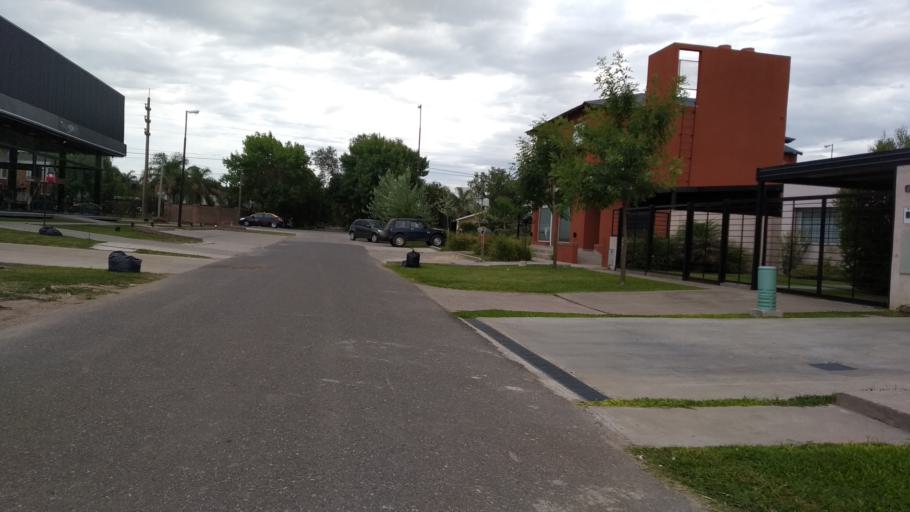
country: AR
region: Santa Fe
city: Funes
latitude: -32.9295
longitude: -60.8038
